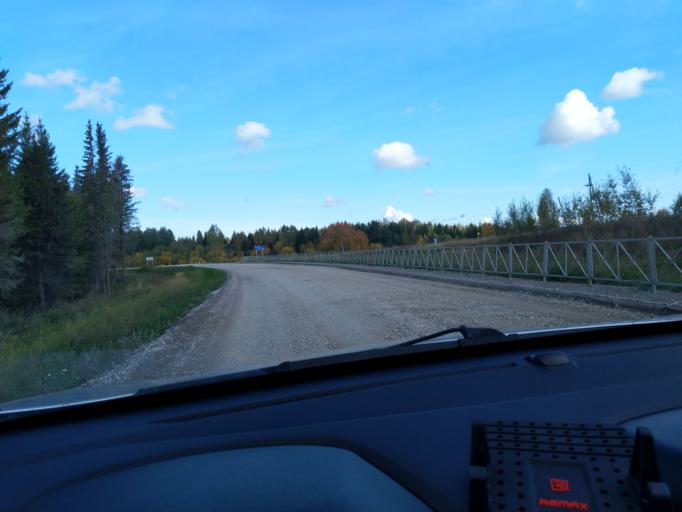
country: RU
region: Perm
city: Usol'ye
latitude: 59.4633
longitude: 56.3673
